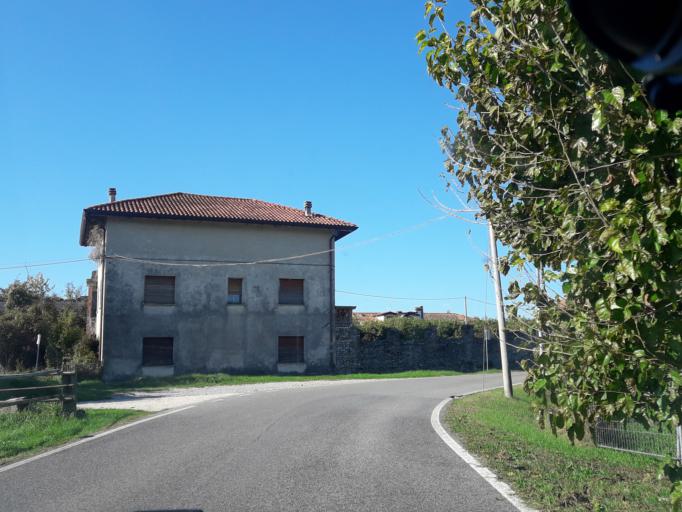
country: IT
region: Friuli Venezia Giulia
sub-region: Provincia di Udine
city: Udine
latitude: 46.0689
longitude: 13.2812
